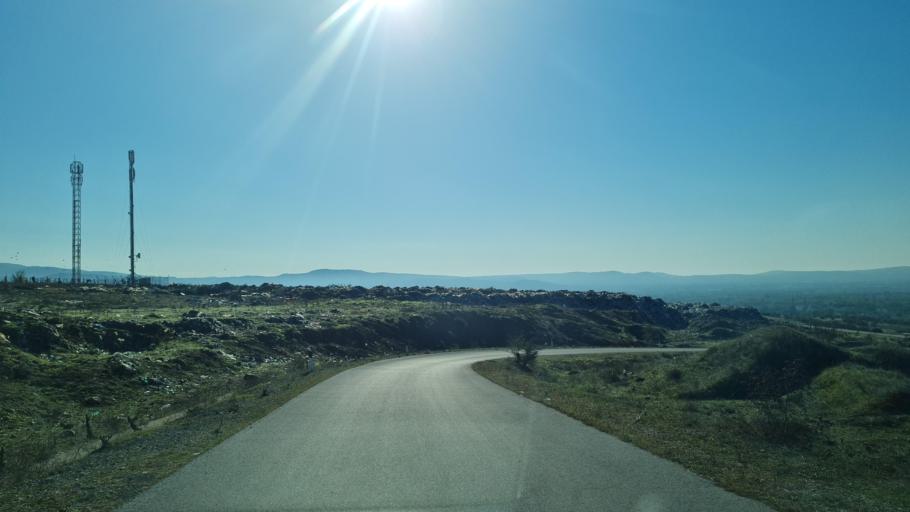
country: MK
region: Bogdanci
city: Bogdanci
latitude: 41.2001
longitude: 22.5614
